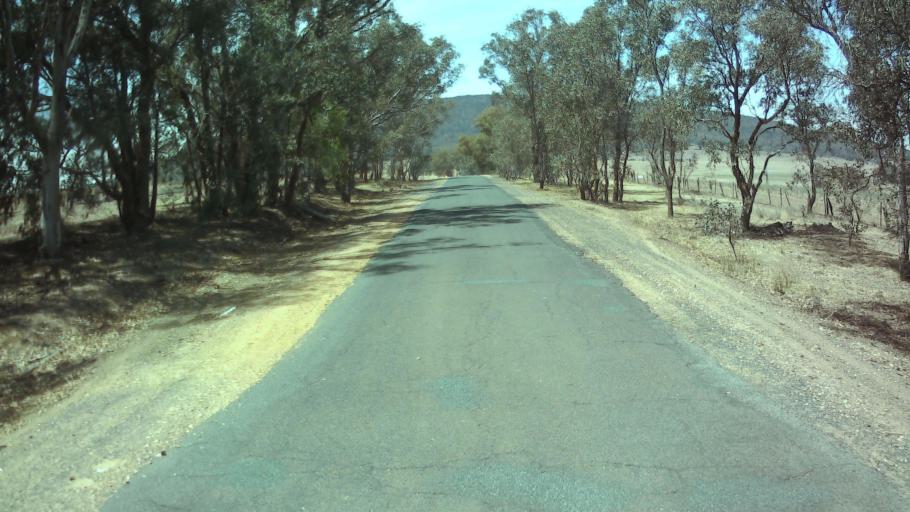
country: AU
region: New South Wales
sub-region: Weddin
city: Grenfell
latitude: -34.0302
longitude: 148.4326
